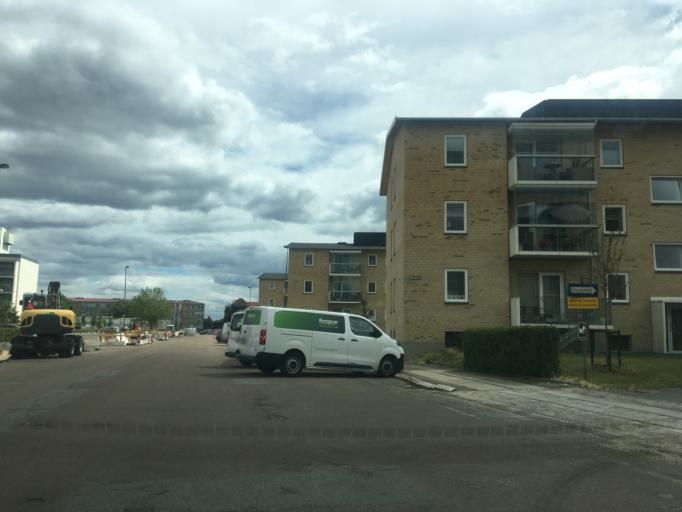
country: DK
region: Capital Region
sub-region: Tarnby Kommune
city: Tarnby
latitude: 55.6410
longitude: 12.6127
